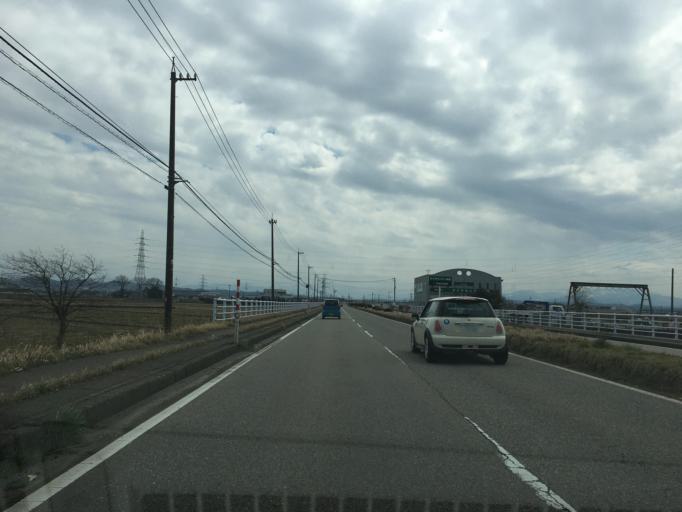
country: JP
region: Toyama
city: Kuragaki-kosugi
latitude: 36.7422
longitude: 137.1298
